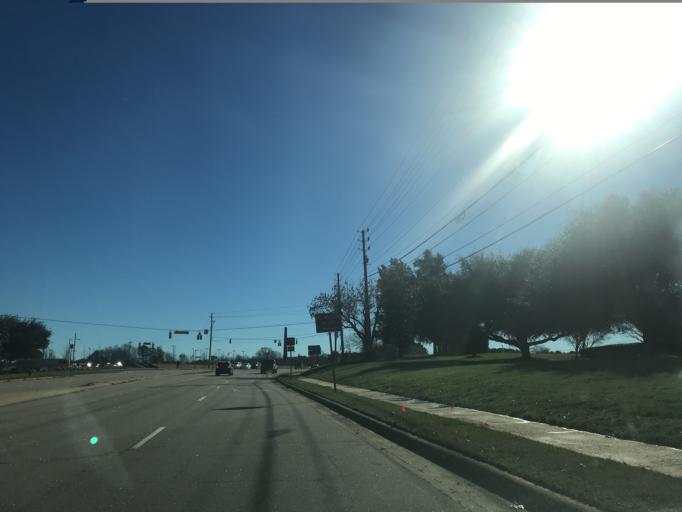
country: US
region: North Carolina
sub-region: Wake County
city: West Raleigh
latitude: 35.8109
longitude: -78.7058
